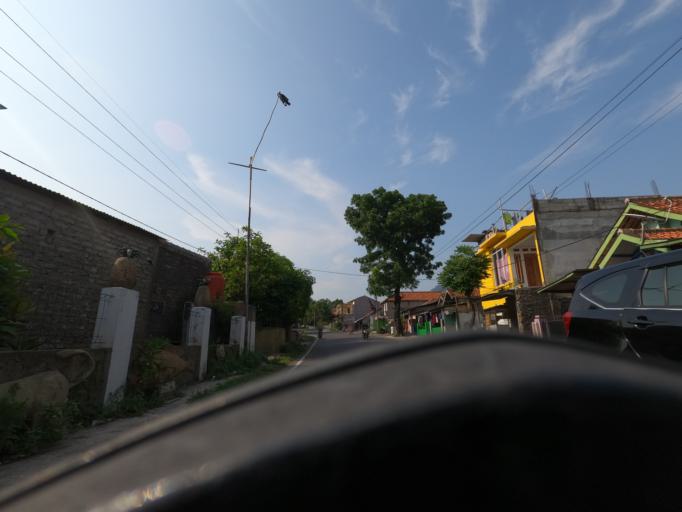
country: ID
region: West Java
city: Lembang
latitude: -6.6165
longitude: 107.7276
